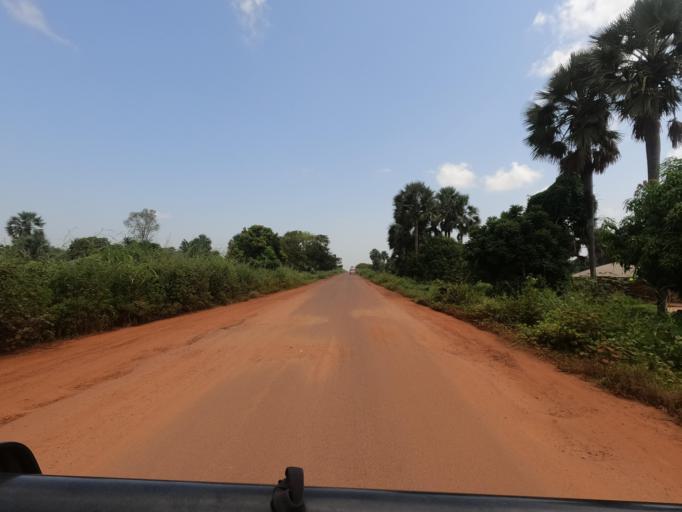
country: GW
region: Oio
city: Bissora
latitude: 12.2944
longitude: -15.7687
